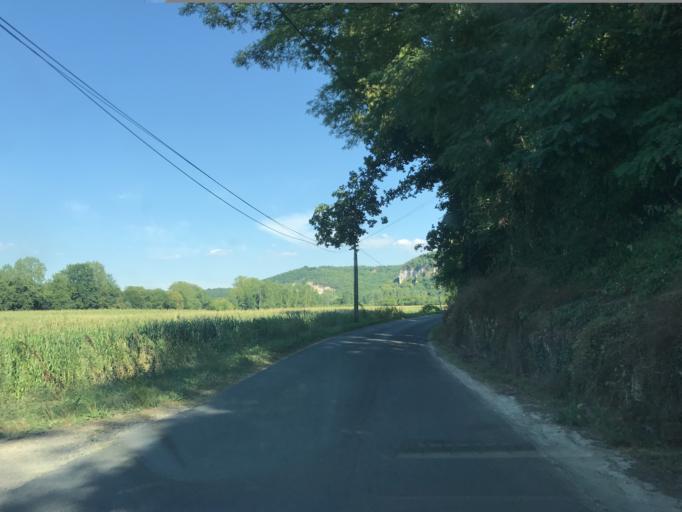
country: FR
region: Aquitaine
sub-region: Departement de la Dordogne
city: Carsac-Aillac
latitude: 44.8238
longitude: 1.2363
